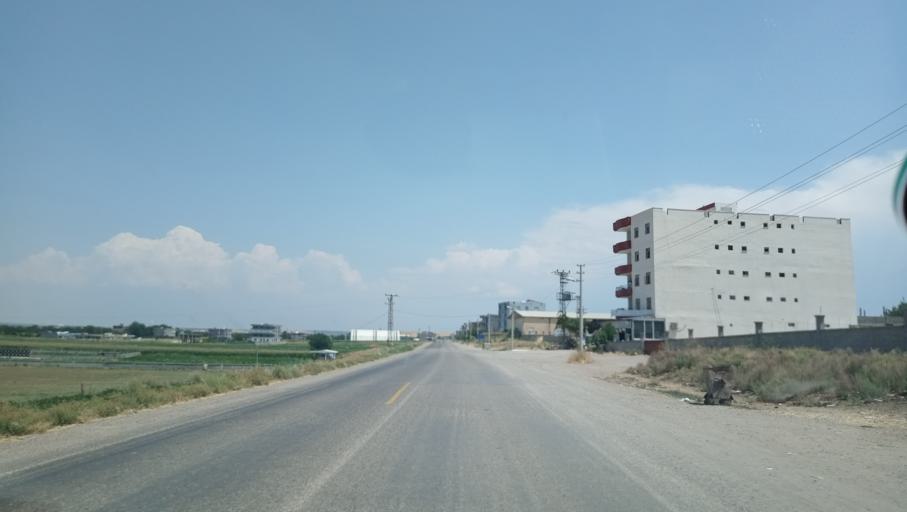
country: TR
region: Diyarbakir
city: Aralik
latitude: 37.8293
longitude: 40.6676
